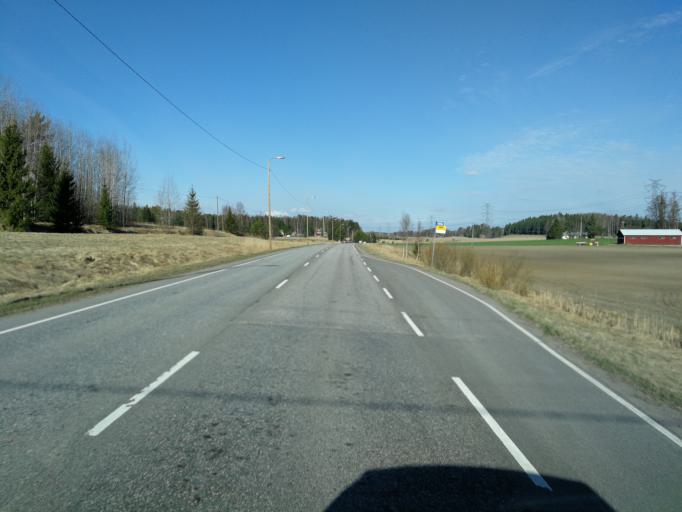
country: FI
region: Uusimaa
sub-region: Helsinki
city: Espoo
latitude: 60.2007
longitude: 24.5363
